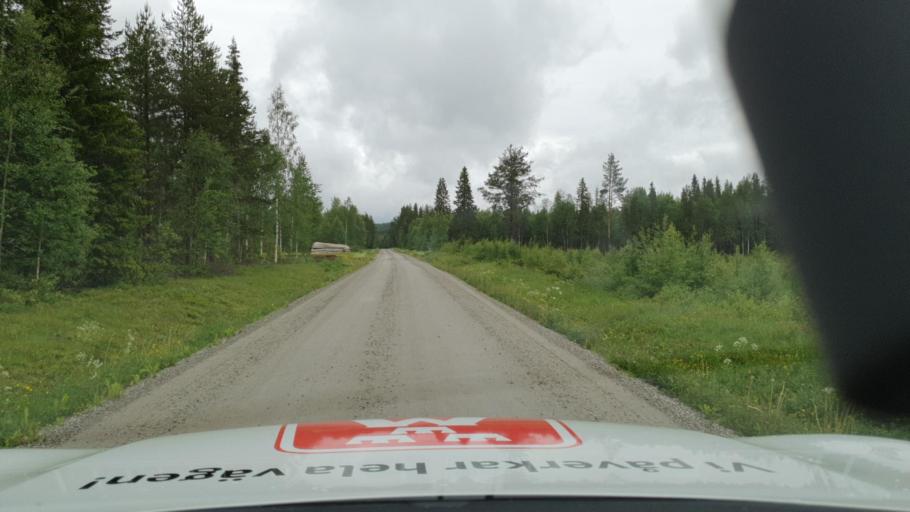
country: SE
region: Vaesterbotten
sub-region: Dorotea Kommun
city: Dorotea
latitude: 64.0216
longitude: 16.7920
